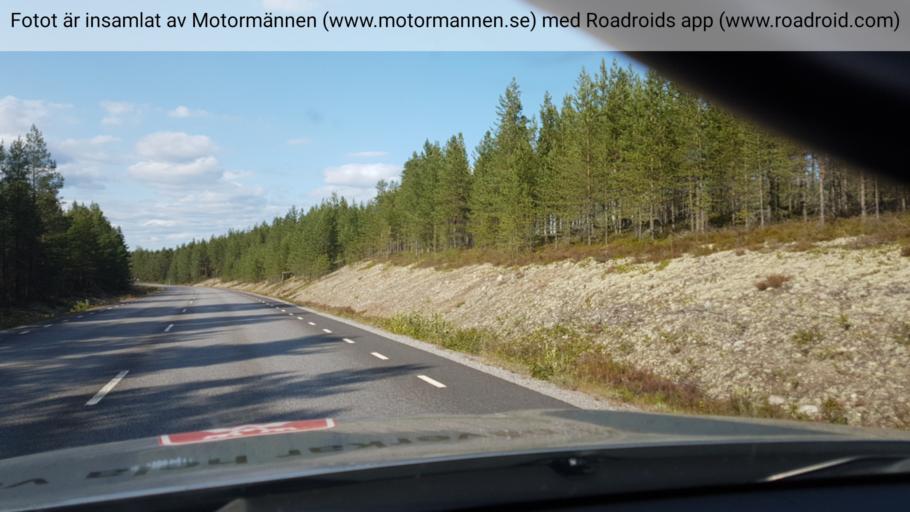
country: SE
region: Norrbotten
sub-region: Pitea Kommun
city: Pitea
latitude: 65.2622
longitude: 21.5380
